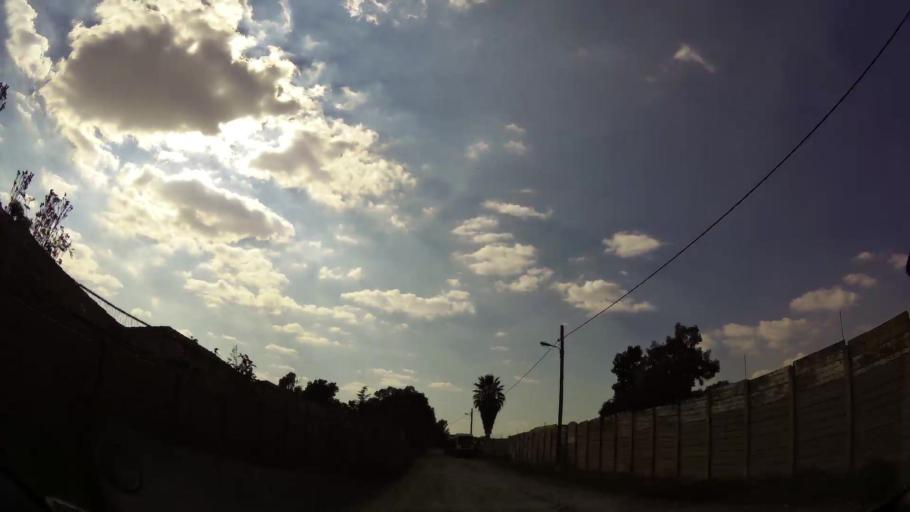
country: ZA
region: Gauteng
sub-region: Ekurhuleni Metropolitan Municipality
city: Benoni
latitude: -26.1028
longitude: 28.3631
